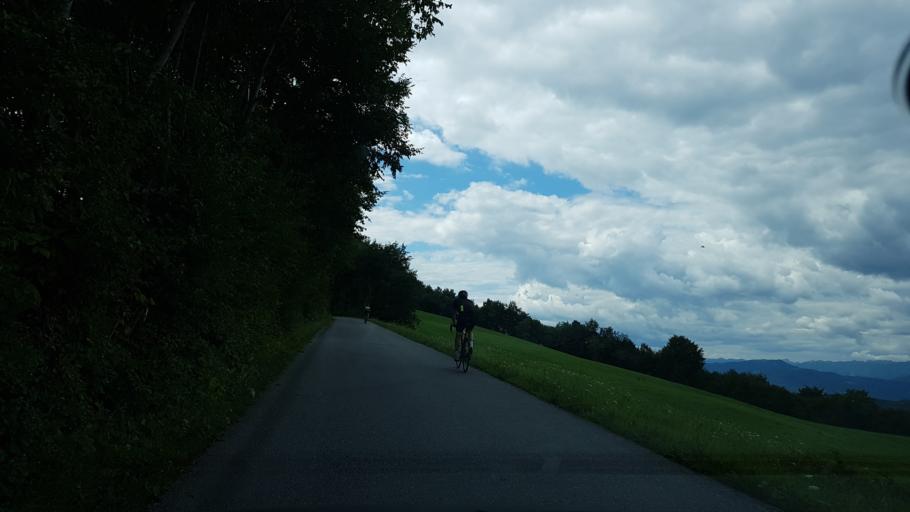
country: SI
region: Kanal
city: Deskle
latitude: 46.0684
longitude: 13.5759
